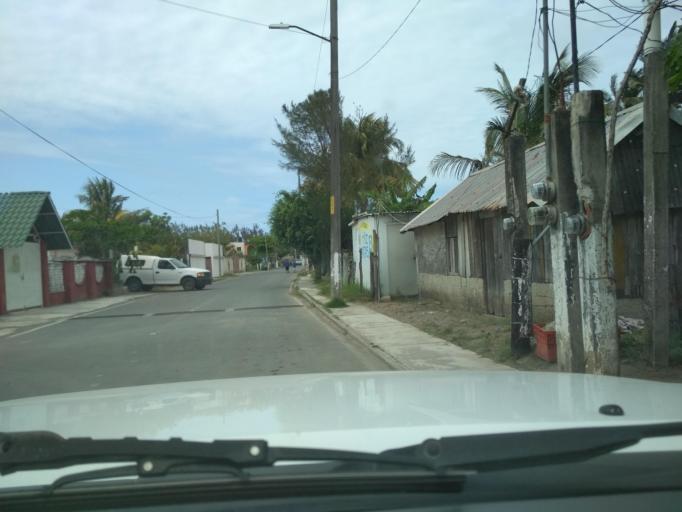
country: MX
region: Veracruz
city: Anton Lizardo
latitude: 19.0359
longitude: -95.9697
